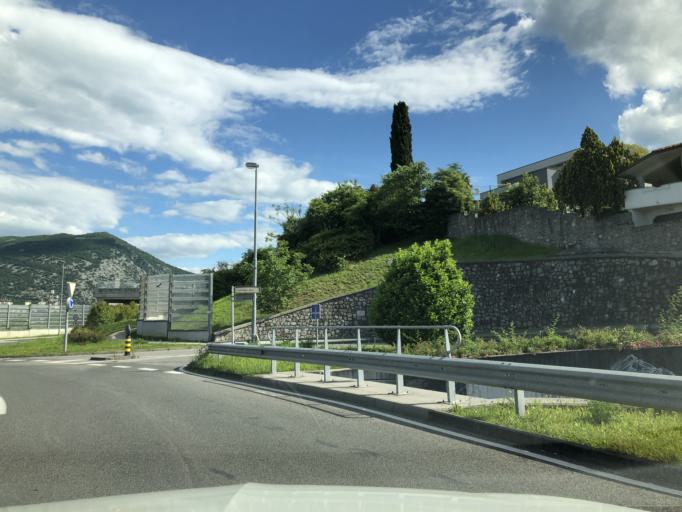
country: SI
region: Nova Gorica
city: Nova Gorica
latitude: 45.9585
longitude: 13.6528
